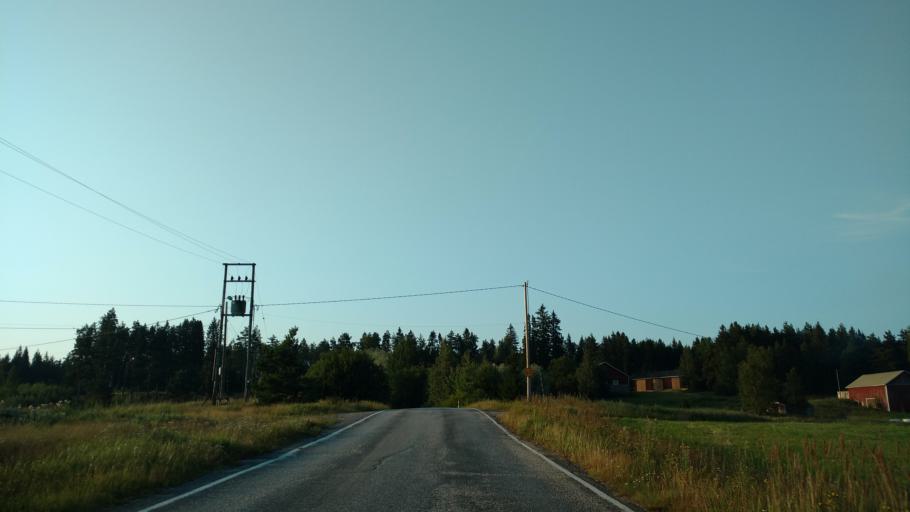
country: FI
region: Varsinais-Suomi
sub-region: Salo
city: Saerkisalo
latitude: 60.1782
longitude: 22.9660
